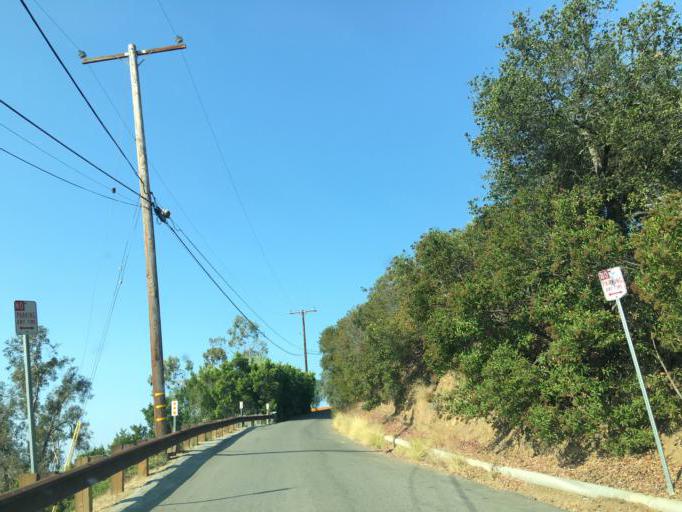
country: US
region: California
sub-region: Los Angeles County
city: Las Flores
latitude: 34.0513
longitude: -118.6442
